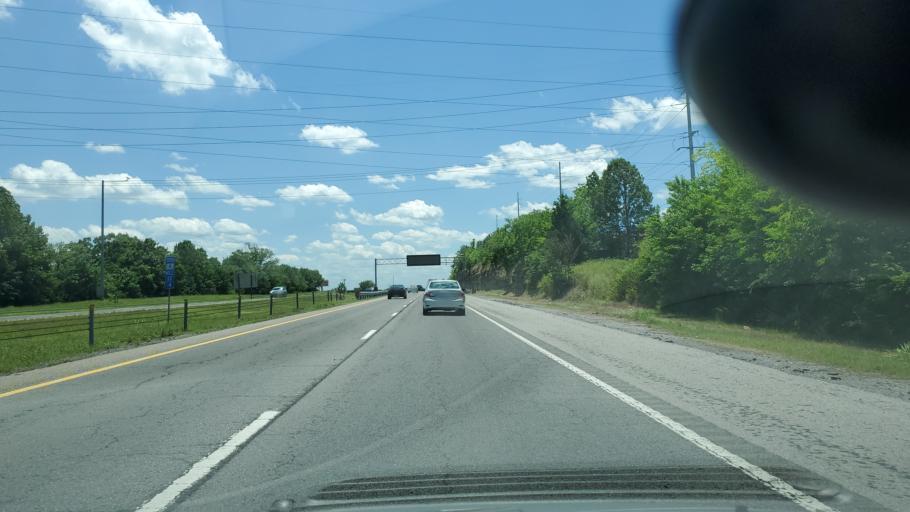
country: US
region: Tennessee
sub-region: Davidson County
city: Nashville
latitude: 36.2113
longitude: -86.7492
